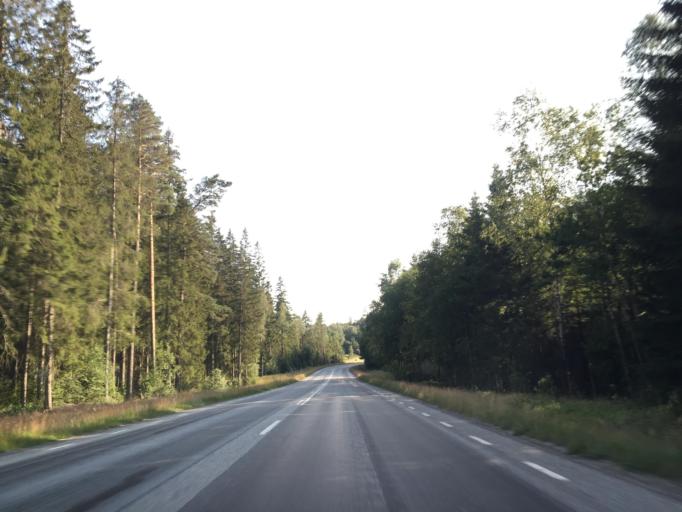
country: SE
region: Vaestra Goetaland
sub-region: Uddevalla Kommun
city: Ljungskile
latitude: 58.0959
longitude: 11.9776
